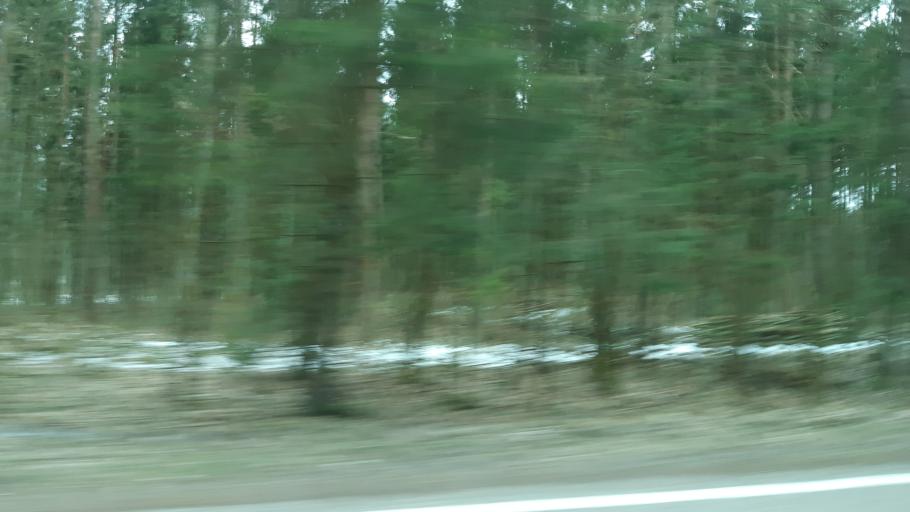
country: PL
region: Podlasie
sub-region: Suwalki
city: Suwalki
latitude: 54.2966
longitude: 22.9585
